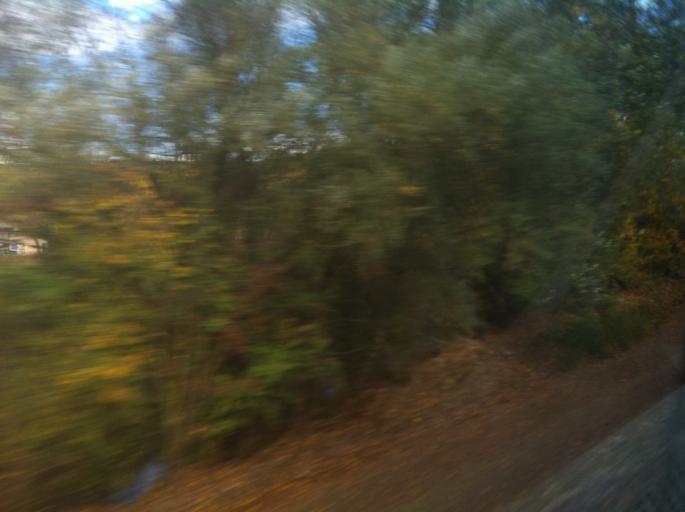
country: ES
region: Castille and Leon
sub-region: Provincia de Burgos
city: Briviesca
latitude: 42.5251
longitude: -3.3312
